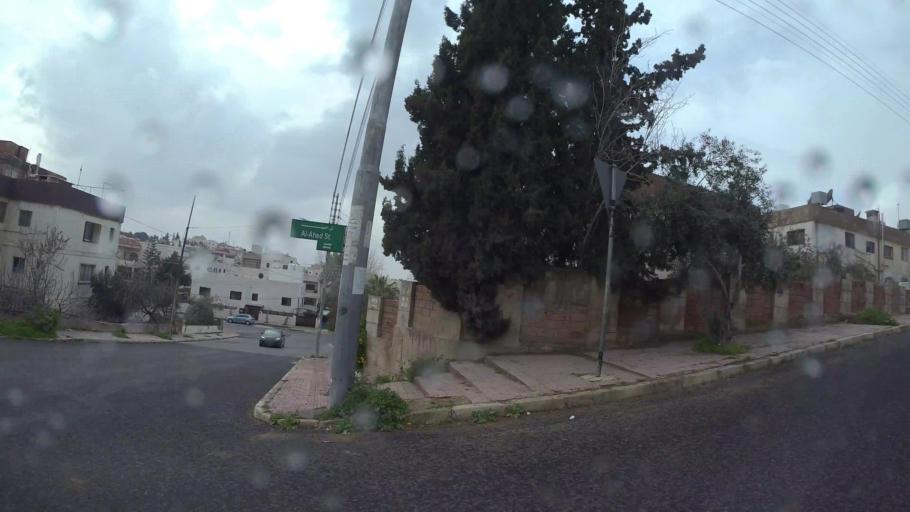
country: JO
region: Amman
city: Umm as Summaq
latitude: 31.8913
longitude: 35.8570
